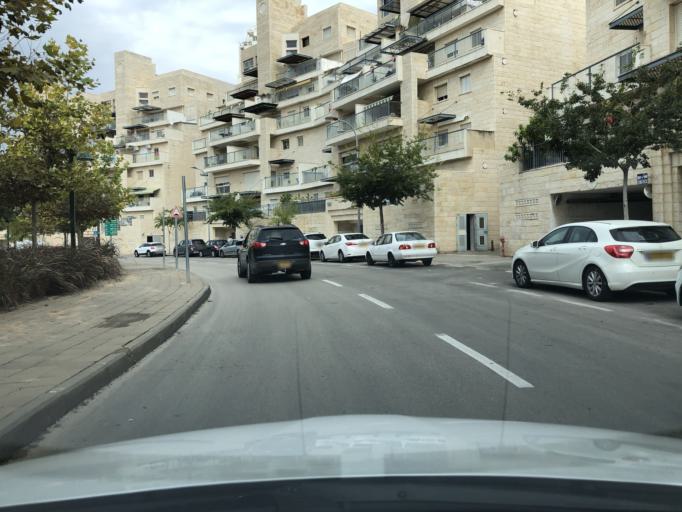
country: IL
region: Central District
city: Modiin
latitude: 31.9116
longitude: 35.0126
